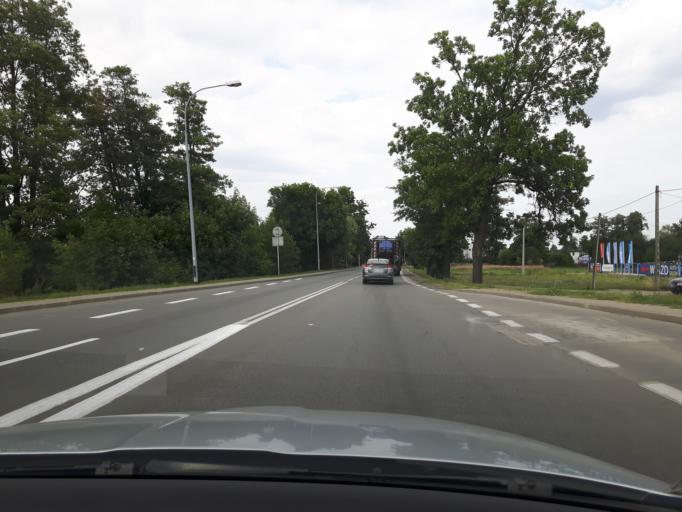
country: PL
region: Masovian Voivodeship
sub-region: Powiat legionowski
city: Stanislawow Pierwszy
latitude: 52.3497
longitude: 21.0293
